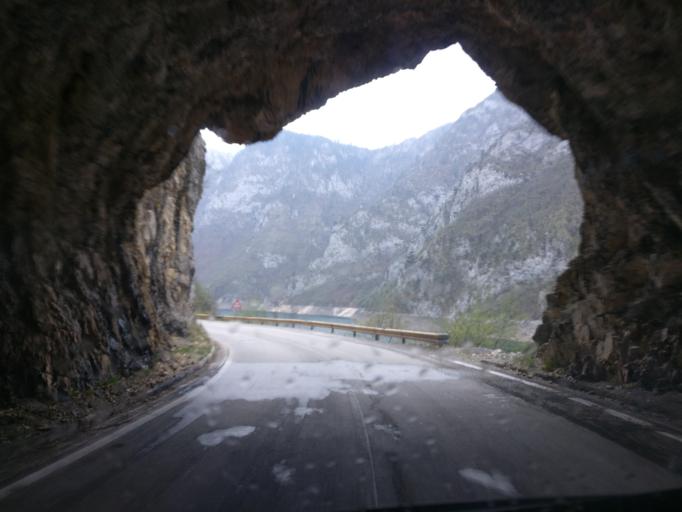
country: ME
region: Opstina Pluzine
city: Pluzine
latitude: 43.2330
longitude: 18.8451
